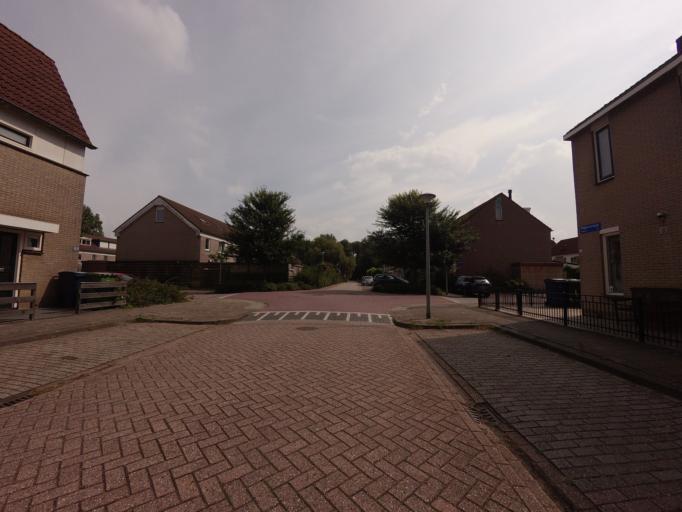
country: NL
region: Flevoland
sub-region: Gemeente Almere
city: Almere Stad
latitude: 52.3802
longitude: 5.1959
